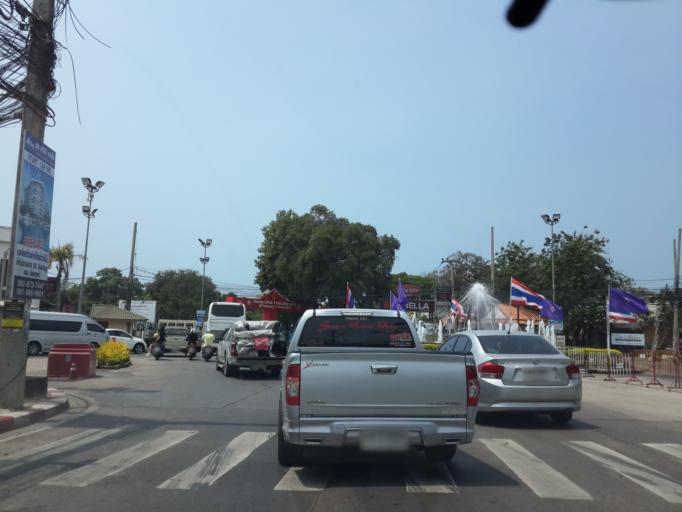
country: TH
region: Chon Buri
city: Phatthaya
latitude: 12.9509
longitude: 100.8879
